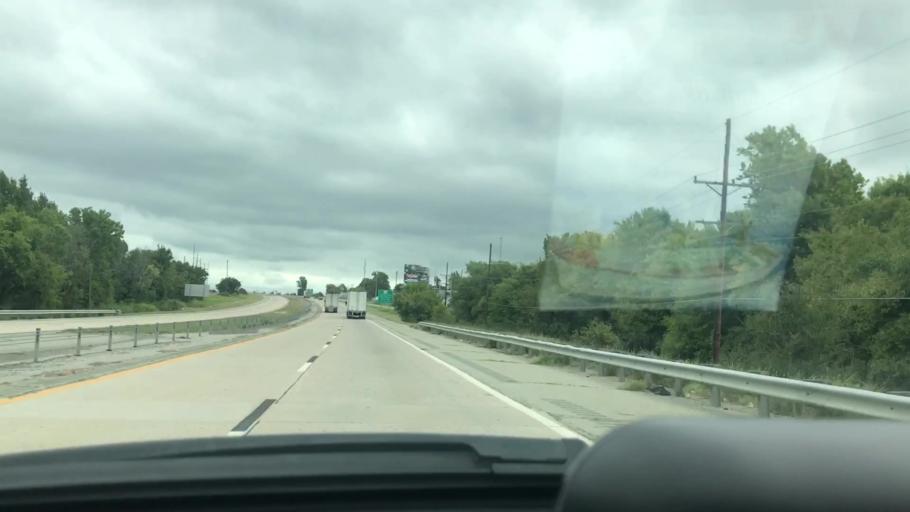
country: US
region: Oklahoma
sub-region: McIntosh County
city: Eufaula
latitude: 35.3515
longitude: -95.5778
